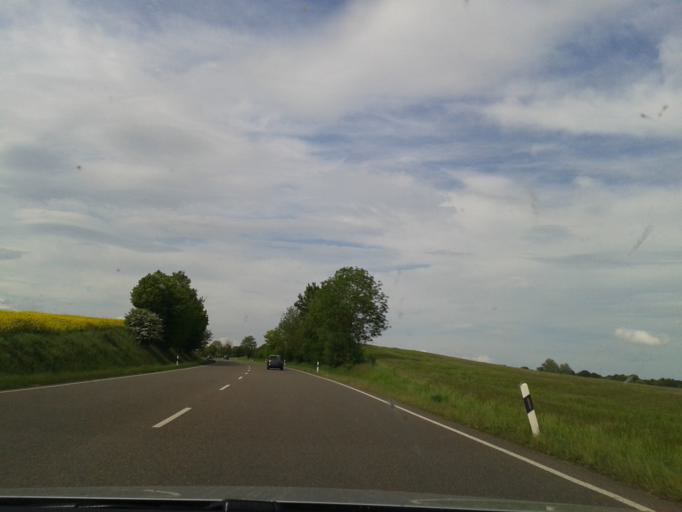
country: DE
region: Hesse
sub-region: Regierungsbezirk Kassel
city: Korbach
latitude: 51.2550
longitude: 8.9038
